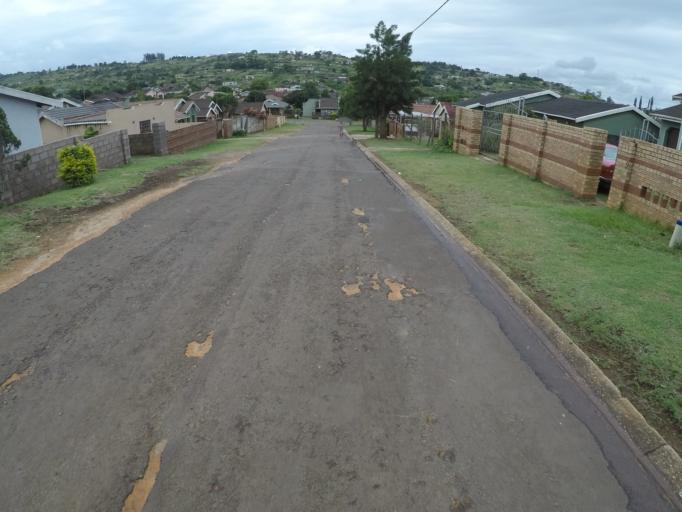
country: ZA
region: KwaZulu-Natal
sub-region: uThungulu District Municipality
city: Empangeni
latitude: -28.7755
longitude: 31.8495
